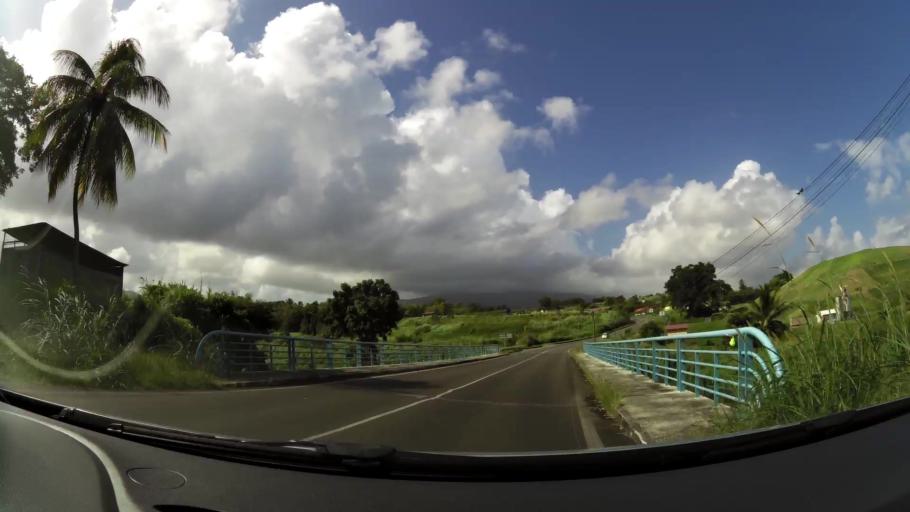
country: MQ
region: Martinique
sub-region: Martinique
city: Le Lorrain
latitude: 14.8410
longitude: -61.0912
